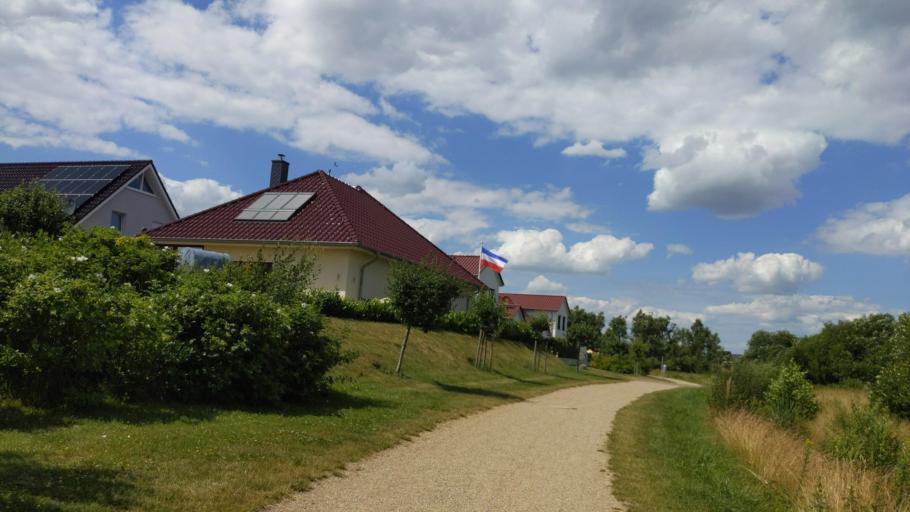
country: DE
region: Schleswig-Holstein
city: Neustadt in Holstein
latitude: 54.1072
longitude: 10.8372
